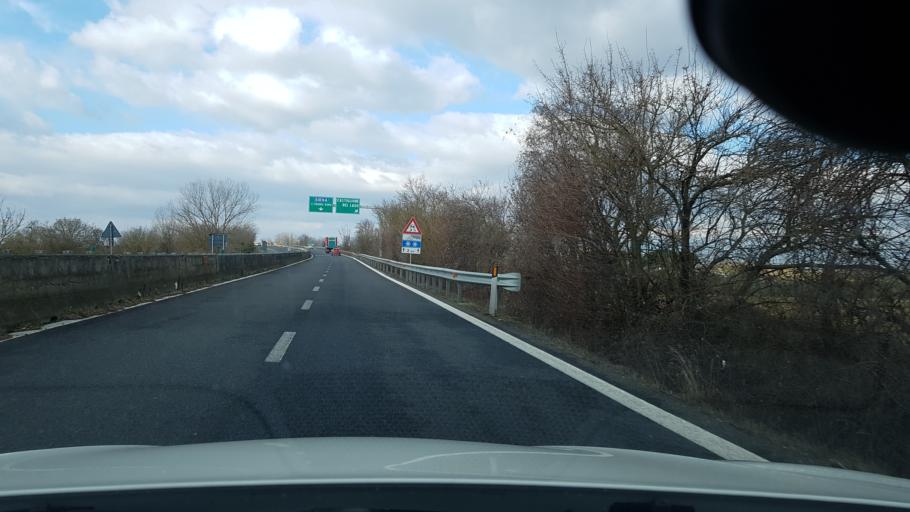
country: IT
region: Tuscany
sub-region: Province of Arezzo
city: Terontola
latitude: 43.1894
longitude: 12.0193
